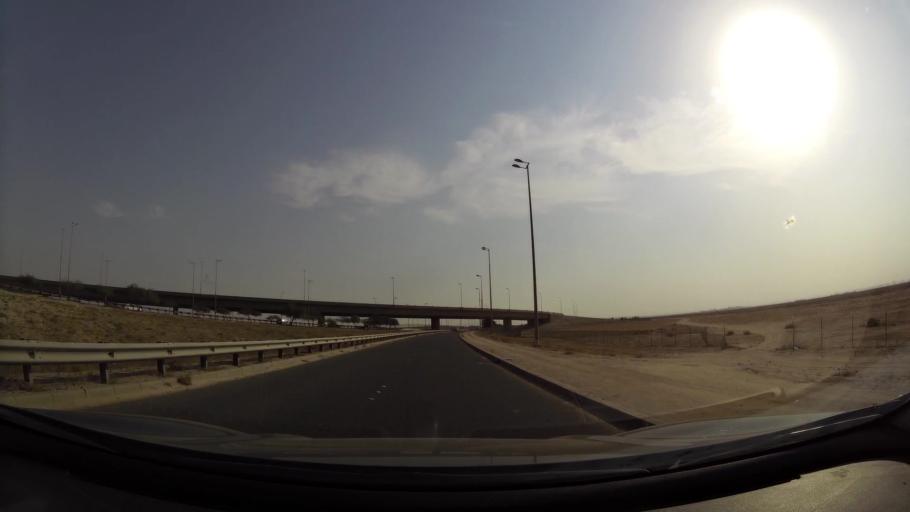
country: KW
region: Al Farwaniyah
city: Janub as Surrah
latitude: 29.1784
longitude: 47.9944
